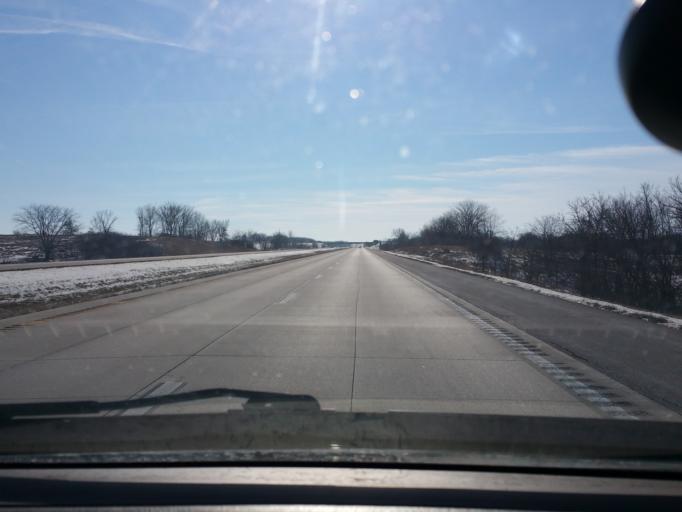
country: US
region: Missouri
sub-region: Daviess County
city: Gallatin
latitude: 40.0055
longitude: -94.0966
